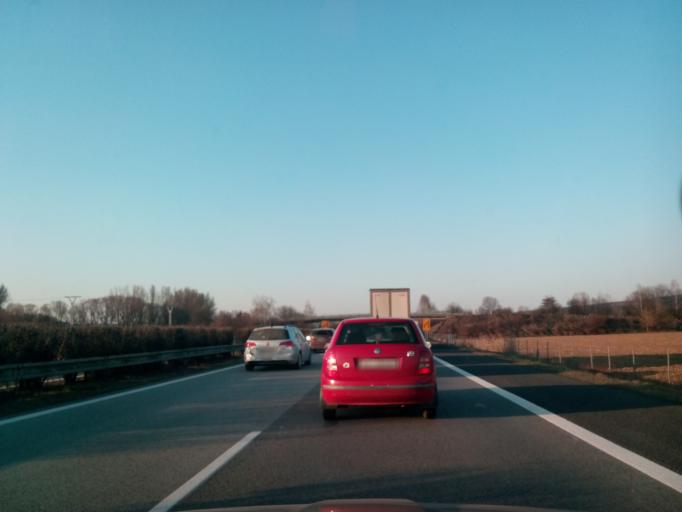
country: SK
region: Presovsky
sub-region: Okres Presov
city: Presov
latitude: 48.9112
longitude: 21.2510
